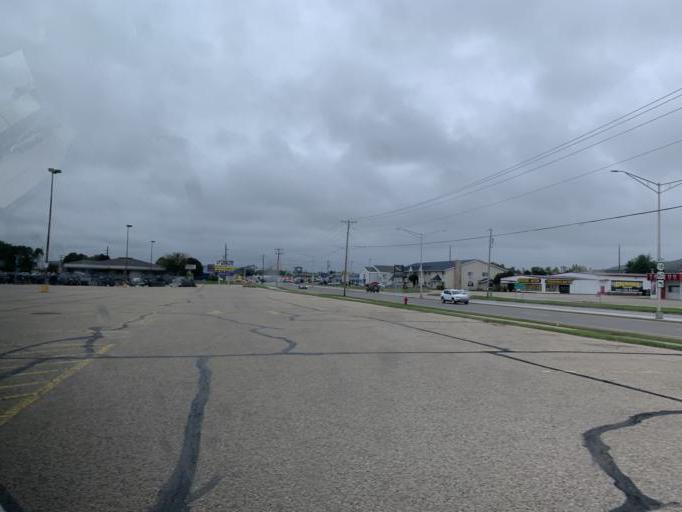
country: US
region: Wisconsin
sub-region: Crawford County
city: Prairie du Chien
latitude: 43.0268
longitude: -91.1258
